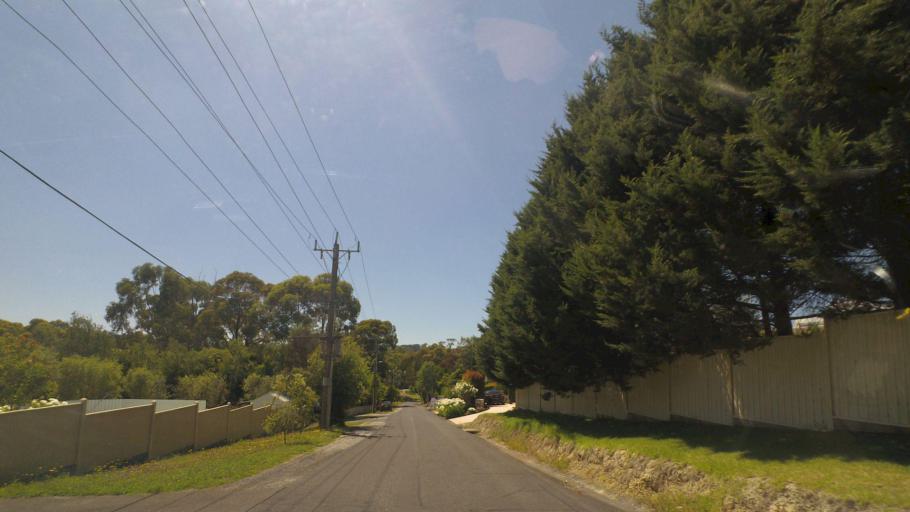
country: AU
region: Victoria
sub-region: Maroondah
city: Warranwood
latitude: -37.7804
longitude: 145.2380
